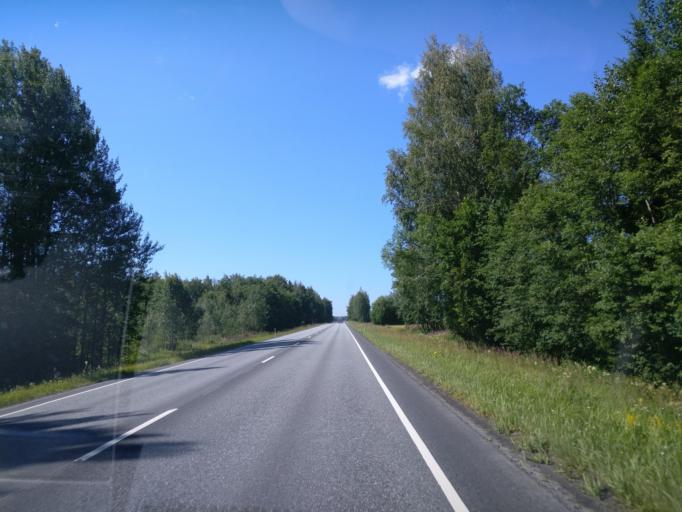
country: FI
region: Satakunta
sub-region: Pori
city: Nakkila
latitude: 61.4582
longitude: 22.0318
